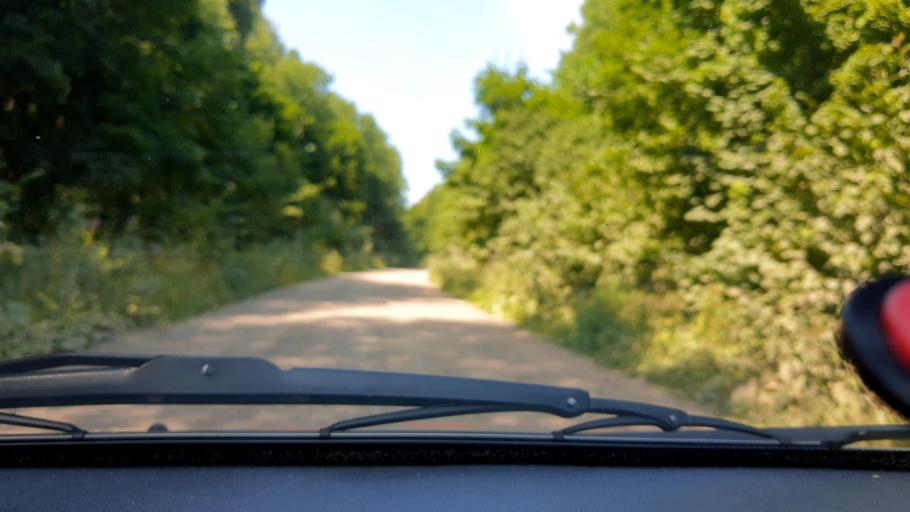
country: RU
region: Bashkortostan
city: Karmaskaly
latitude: 54.3837
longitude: 55.8959
